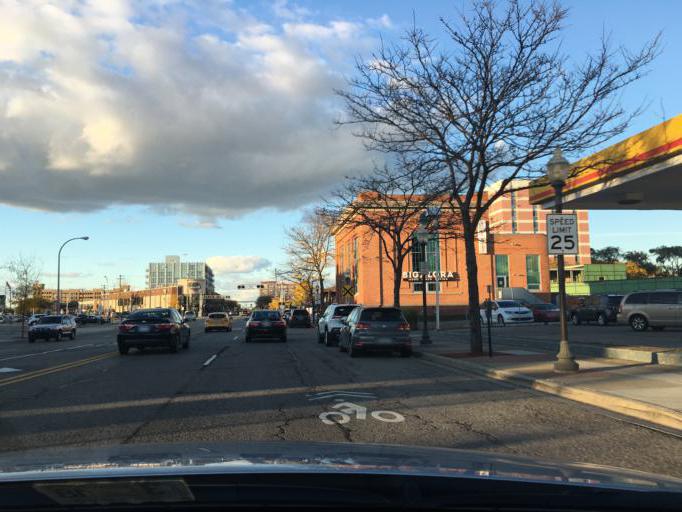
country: US
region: Michigan
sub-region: Oakland County
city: Royal Oak
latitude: 42.4836
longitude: -83.1440
